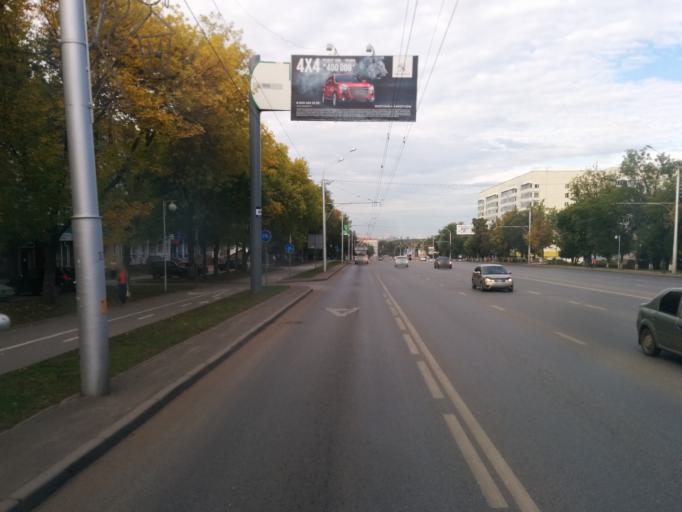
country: RU
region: Bashkortostan
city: Ufa
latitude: 54.7920
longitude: 56.0367
